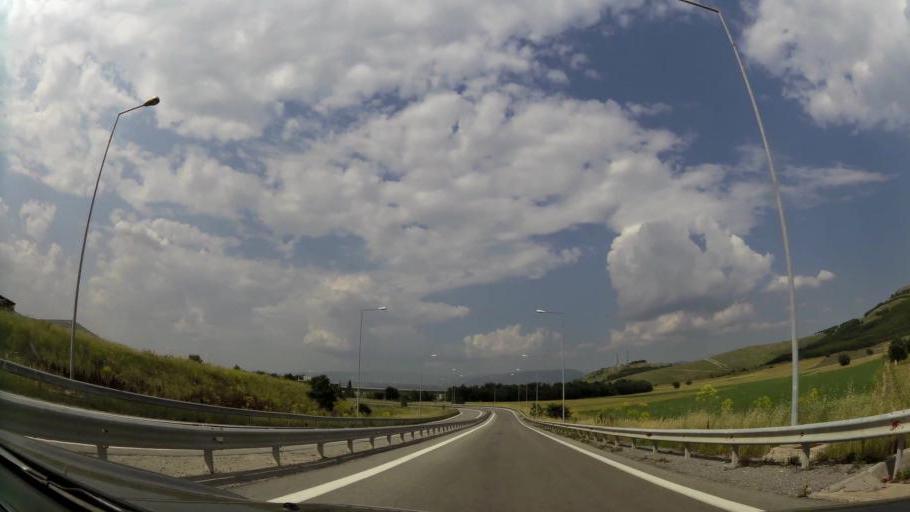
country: GR
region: West Macedonia
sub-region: Nomos Kozanis
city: Koila
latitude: 40.3479
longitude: 21.8072
